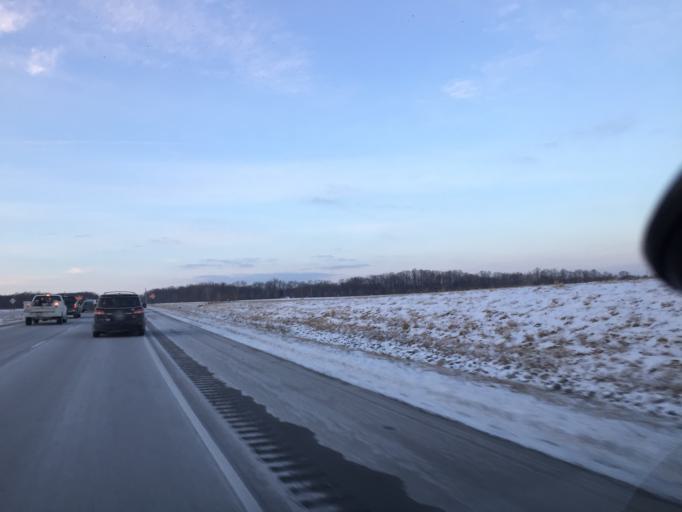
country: US
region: Indiana
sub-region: Monroe County
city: Bloomington
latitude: 39.1903
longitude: -86.5690
